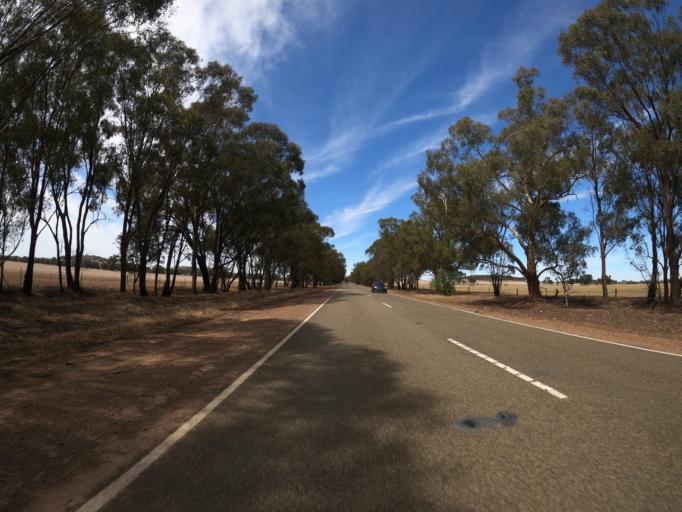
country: AU
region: Victoria
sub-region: Benalla
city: Benalla
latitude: -36.3119
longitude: 145.9583
